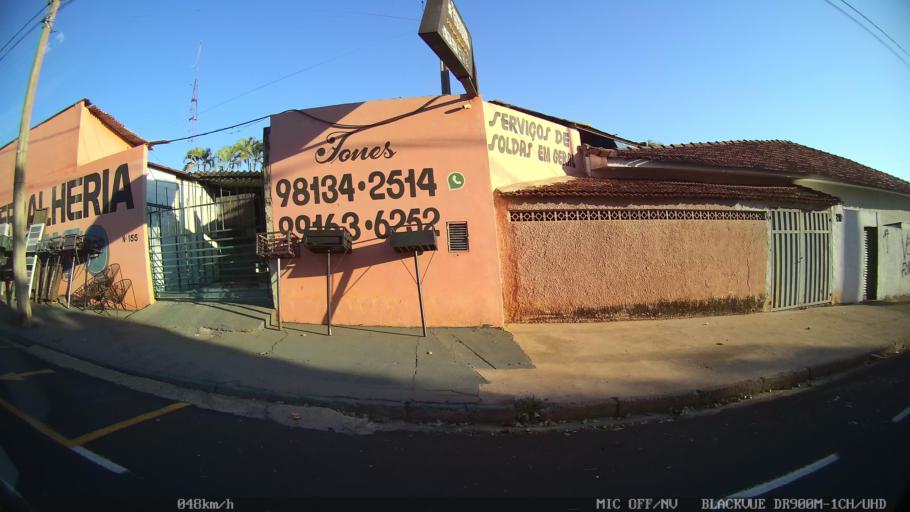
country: BR
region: Sao Paulo
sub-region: Sao Jose Do Rio Preto
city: Sao Jose do Rio Preto
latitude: -20.7874
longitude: -49.3644
